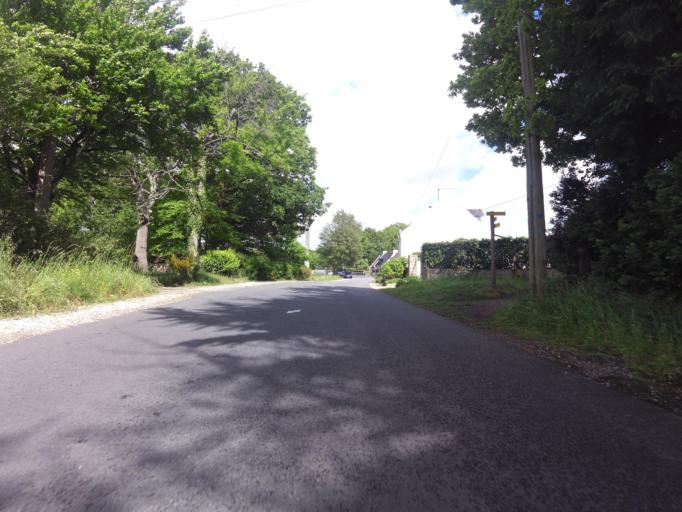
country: FR
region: Brittany
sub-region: Departement du Morbihan
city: Plougoumelen
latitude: 47.6495
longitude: -2.9297
